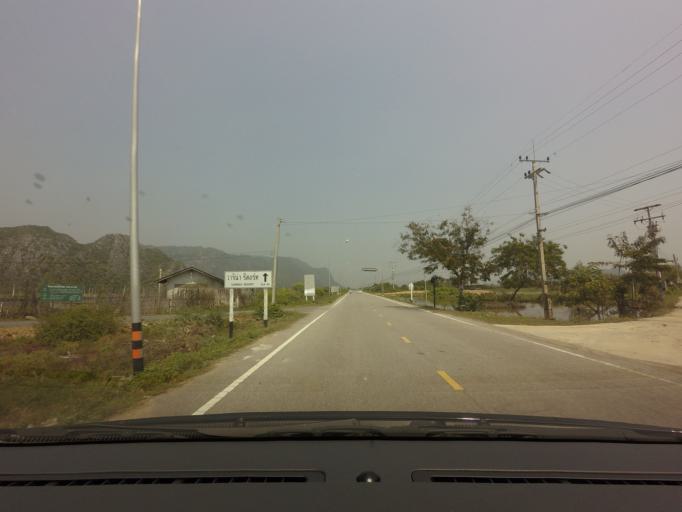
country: TH
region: Prachuap Khiri Khan
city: Kui Buri
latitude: 12.1403
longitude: 99.9641
